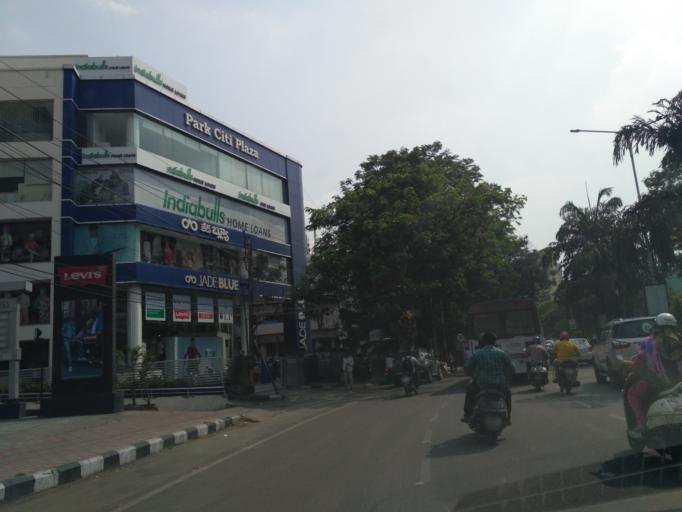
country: IN
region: Telangana
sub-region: Hyderabad
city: Hyderabad
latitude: 17.4222
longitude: 78.4496
